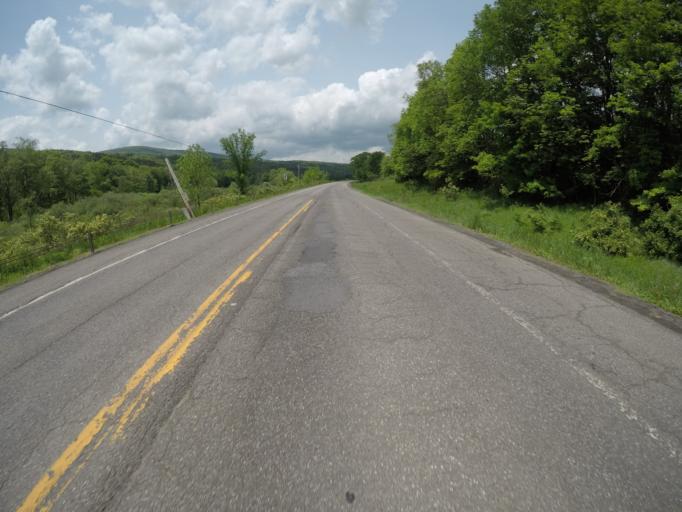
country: US
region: New York
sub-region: Delaware County
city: Stamford
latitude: 42.2299
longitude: -74.5958
